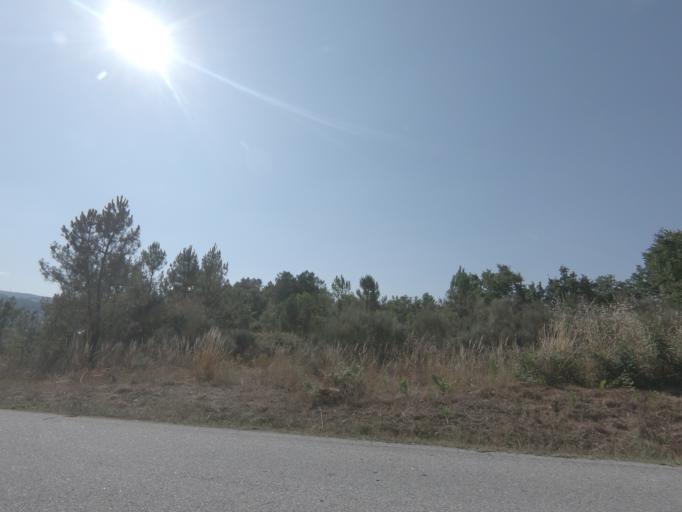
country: PT
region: Viseu
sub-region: Moimenta da Beira
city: Moimenta da Beira
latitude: 40.9798
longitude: -7.5776
